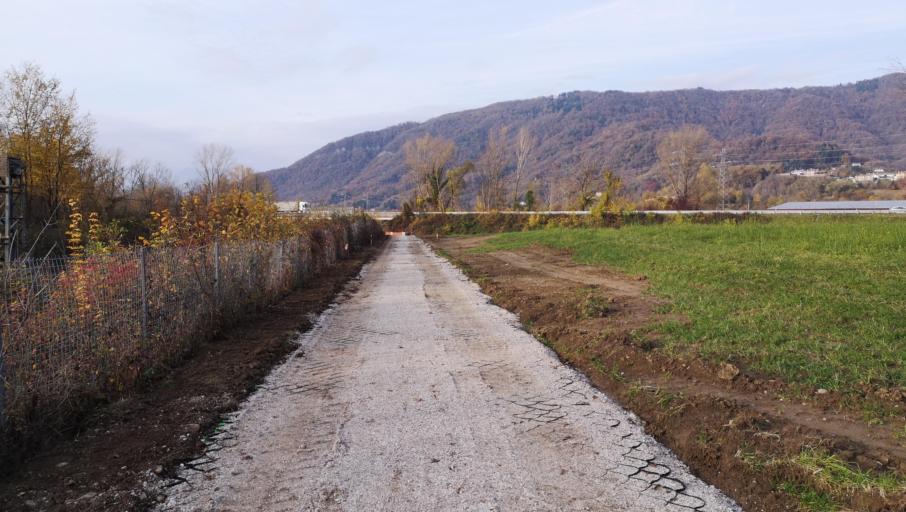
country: IT
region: Friuli Venezia Giulia
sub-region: Provincia di Udine
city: Magnano in Riviera
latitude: 46.2169
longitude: 13.1921
